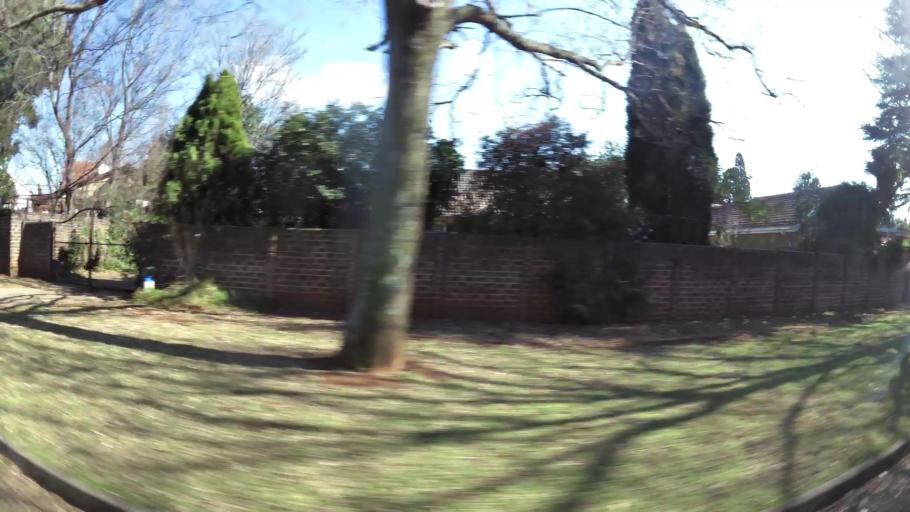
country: ZA
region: Gauteng
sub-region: Ekurhuleni Metropolitan Municipality
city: Benoni
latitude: -26.1445
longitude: 28.3383
